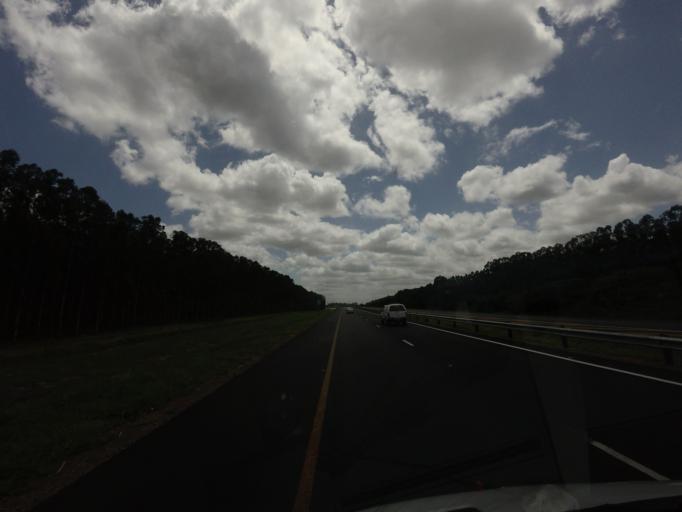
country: ZA
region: KwaZulu-Natal
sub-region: uThungulu District Municipality
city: KwaMbonambi
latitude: -28.5312
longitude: 32.1348
